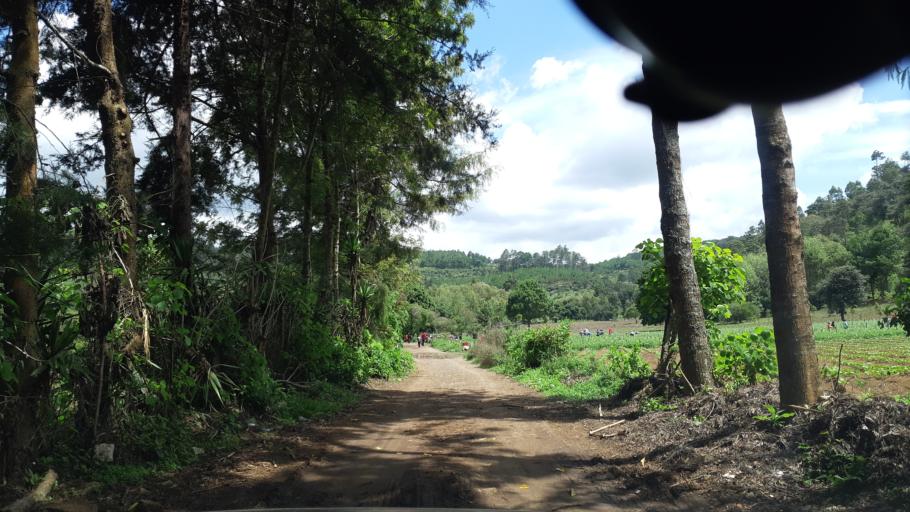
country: GT
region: Chimaltenango
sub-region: Municipio de Chimaltenango
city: Chimaltenango
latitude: 14.6564
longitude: -90.8485
